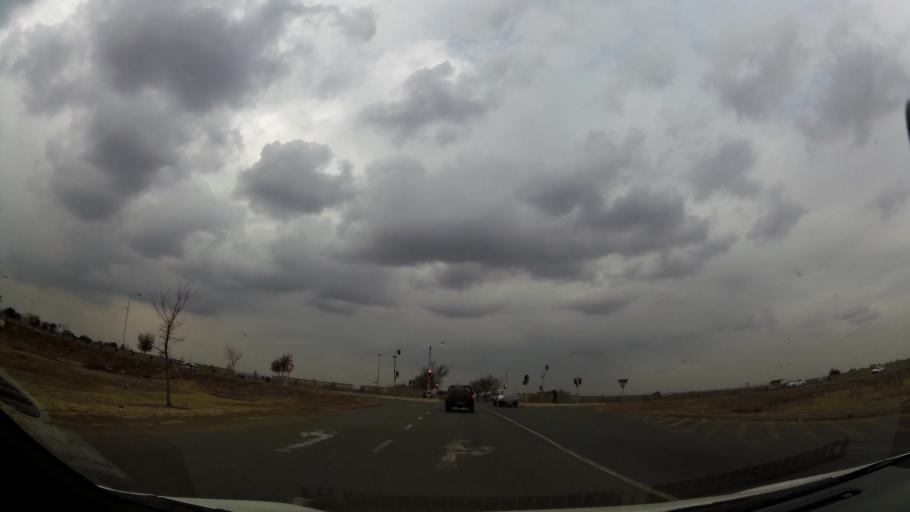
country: ZA
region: Gauteng
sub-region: Ekurhuleni Metropolitan Municipality
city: Germiston
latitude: -26.3799
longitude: 28.1390
